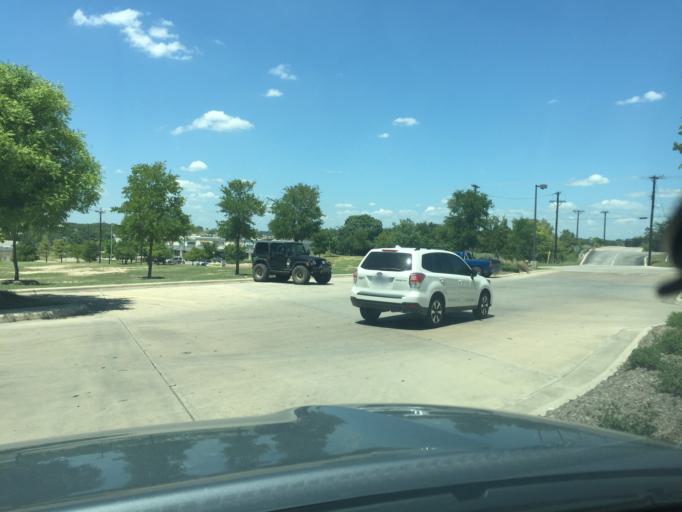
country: US
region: Texas
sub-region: Comal County
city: Bulverde
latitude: 29.7944
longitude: -98.4237
